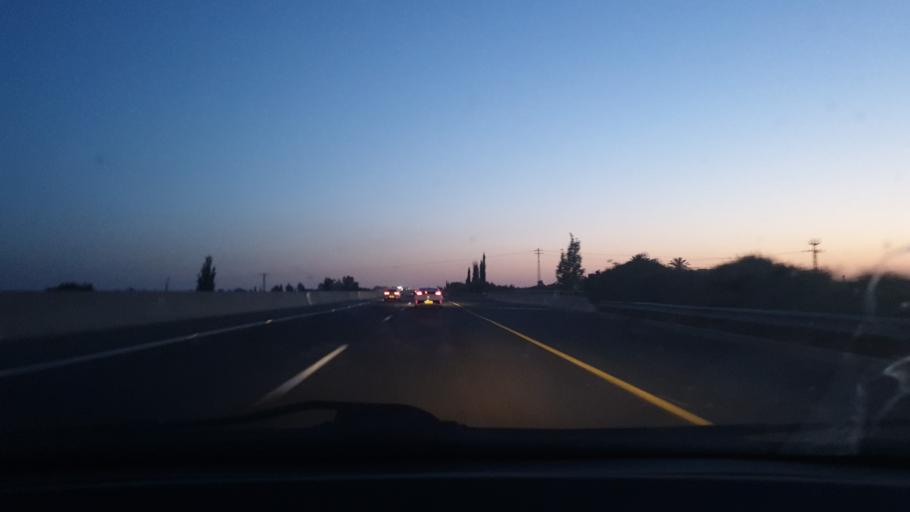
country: IL
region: Central District
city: Gedera
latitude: 31.8037
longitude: 34.8156
